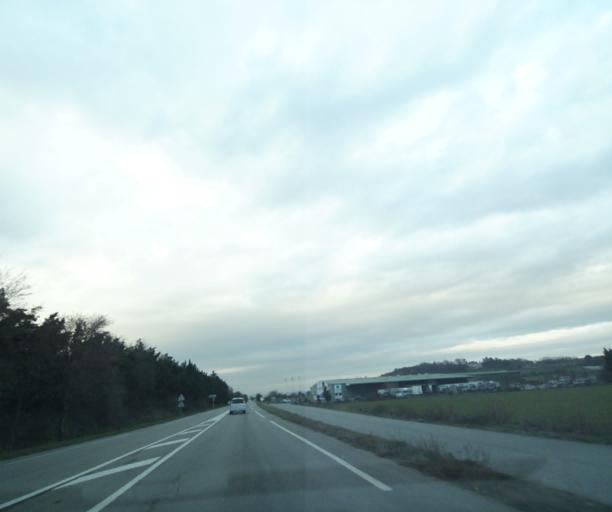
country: FR
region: Rhone-Alpes
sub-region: Departement de la Drome
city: Bourg-les-Valence
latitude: 44.9758
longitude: 4.8970
